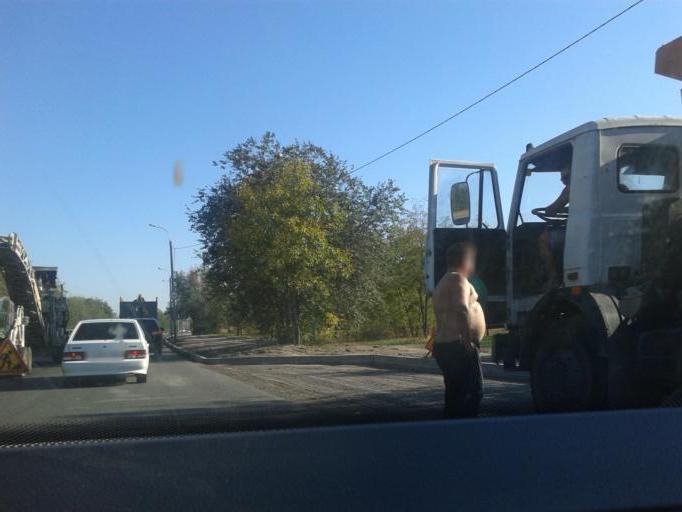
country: RU
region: Volgograd
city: Volgograd
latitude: 48.7616
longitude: 44.5202
